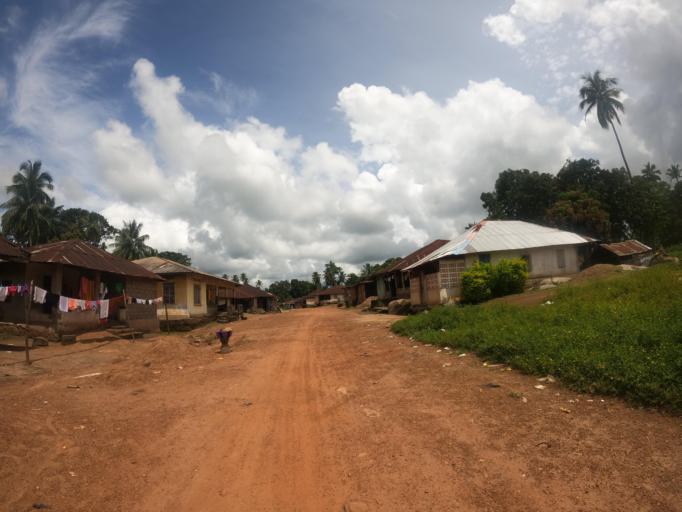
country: SL
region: Northern Province
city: Makeni
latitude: 8.8986
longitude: -12.0586
